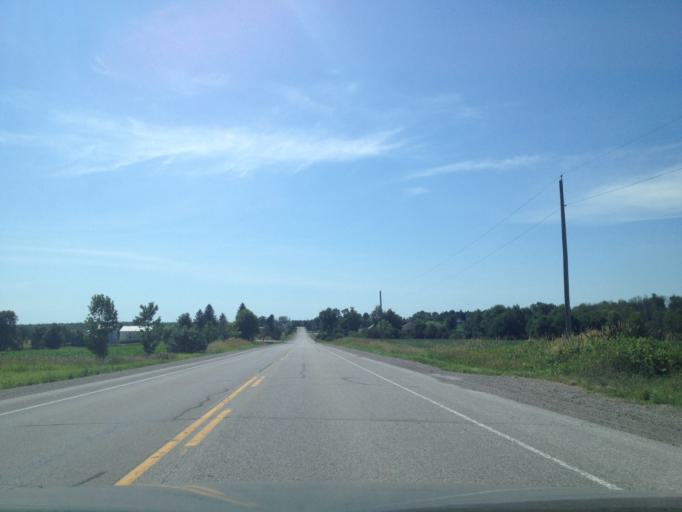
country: CA
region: Ontario
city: Waterloo
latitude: 43.5264
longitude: -80.7300
